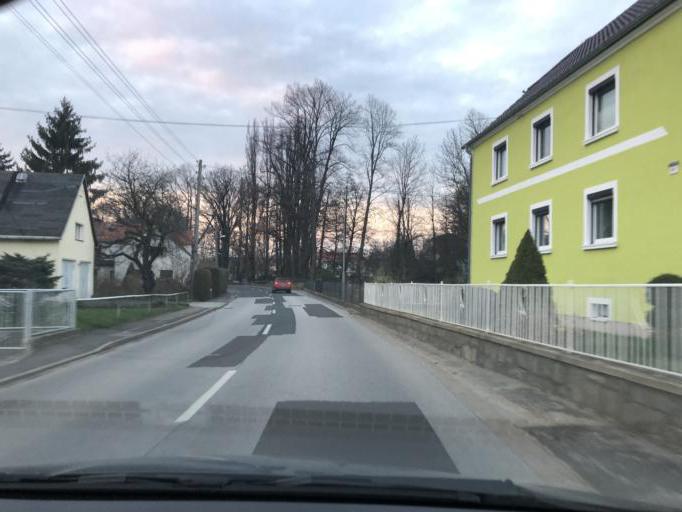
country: DE
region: Saxony
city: Haselbachtal
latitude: 51.2367
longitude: 14.0421
